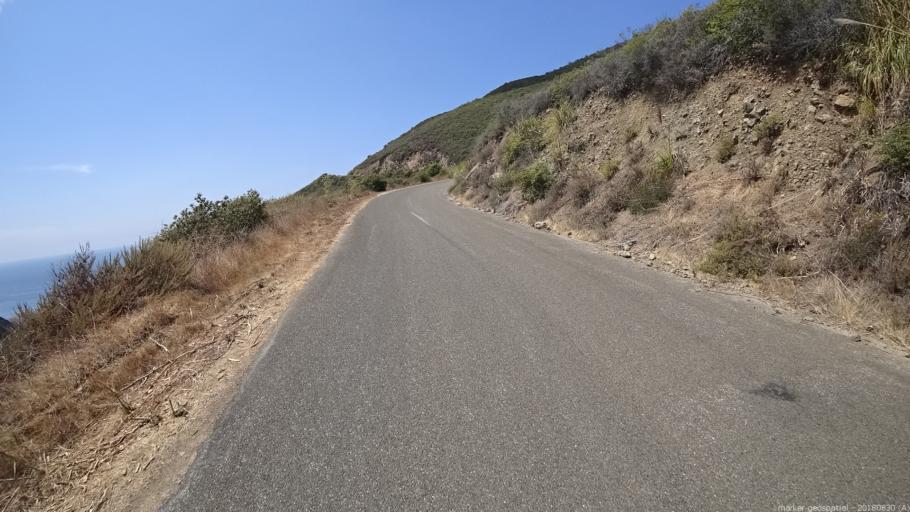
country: US
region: California
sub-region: Monterey County
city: Greenfield
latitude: 35.9872
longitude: -121.4859
